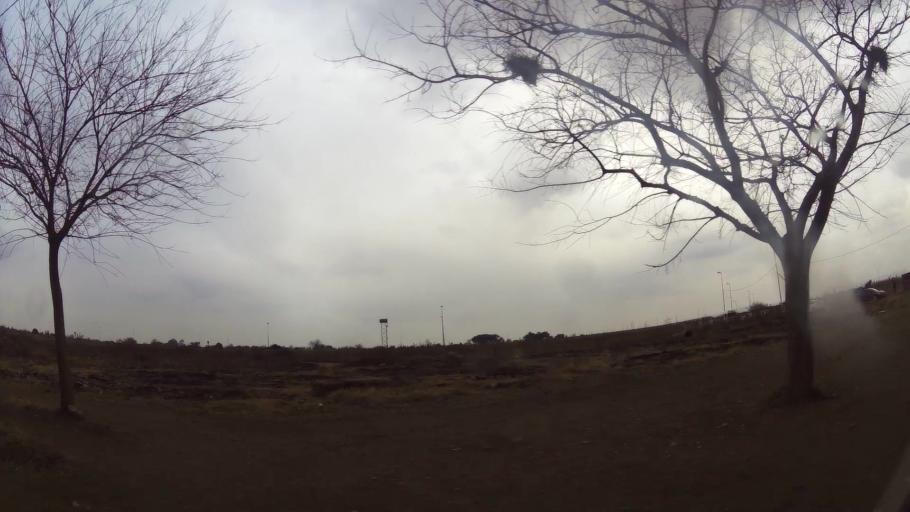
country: ZA
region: Gauteng
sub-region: Ekurhuleni Metropolitan Municipality
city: Germiston
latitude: -26.3690
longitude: 28.1434
